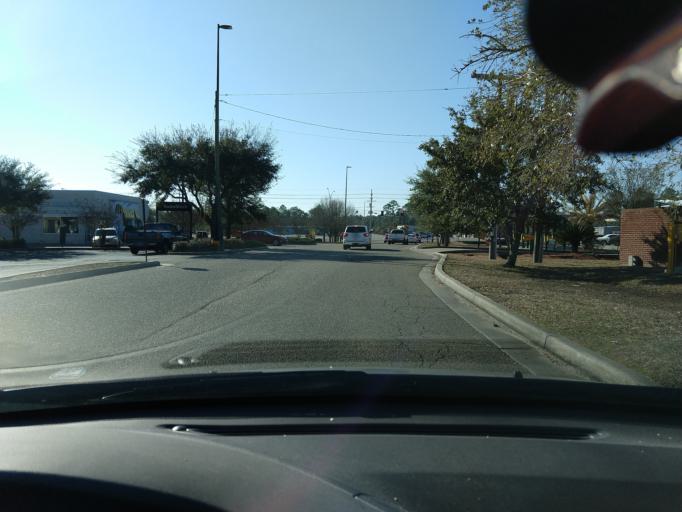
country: US
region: Mississippi
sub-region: Jackson County
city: Gulf Park Estates
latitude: 30.4101
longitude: -88.7595
